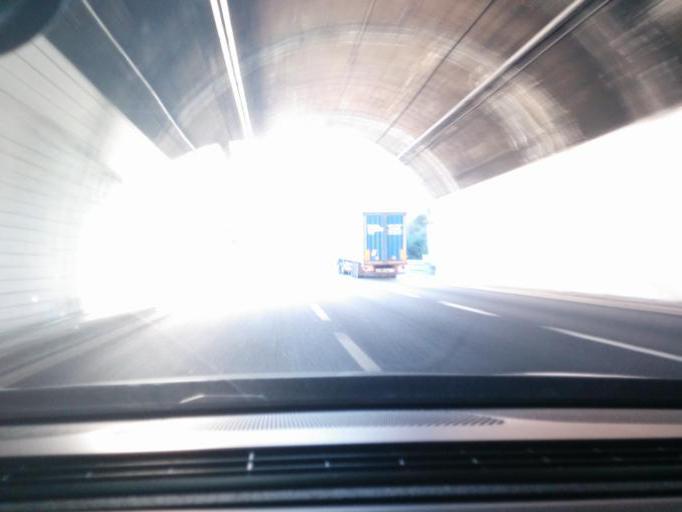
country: IT
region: Liguria
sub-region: Provincia di Genova
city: Cogoleto
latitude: 44.3903
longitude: 8.6320
